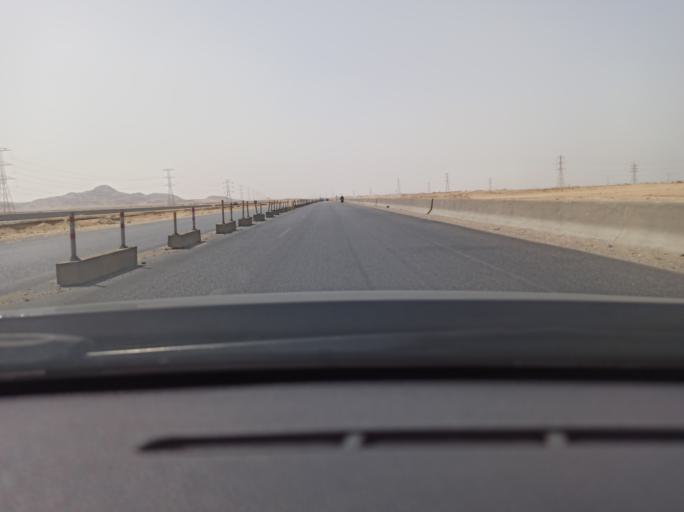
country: EG
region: Muhafazat Bani Suwayf
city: Bush
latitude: 29.1416
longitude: 31.2289
